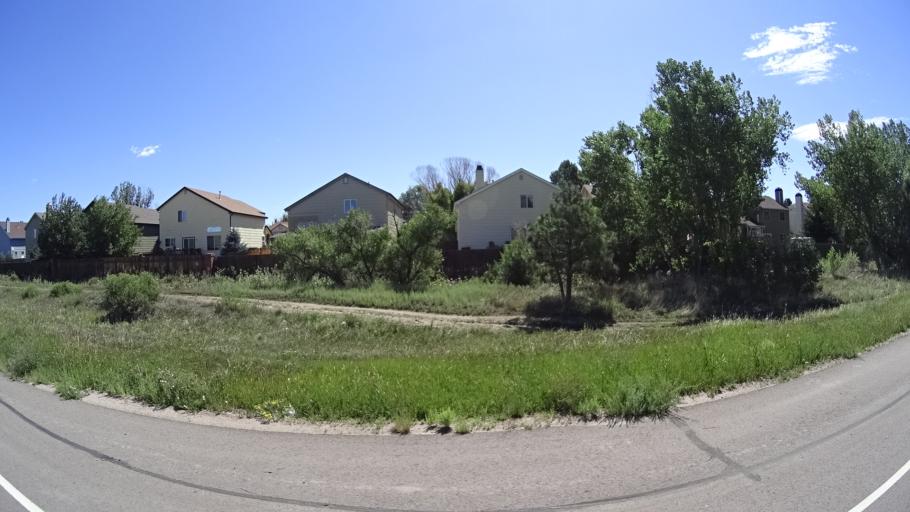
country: US
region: Colorado
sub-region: El Paso County
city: Security-Widefield
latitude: 38.7659
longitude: -104.6595
